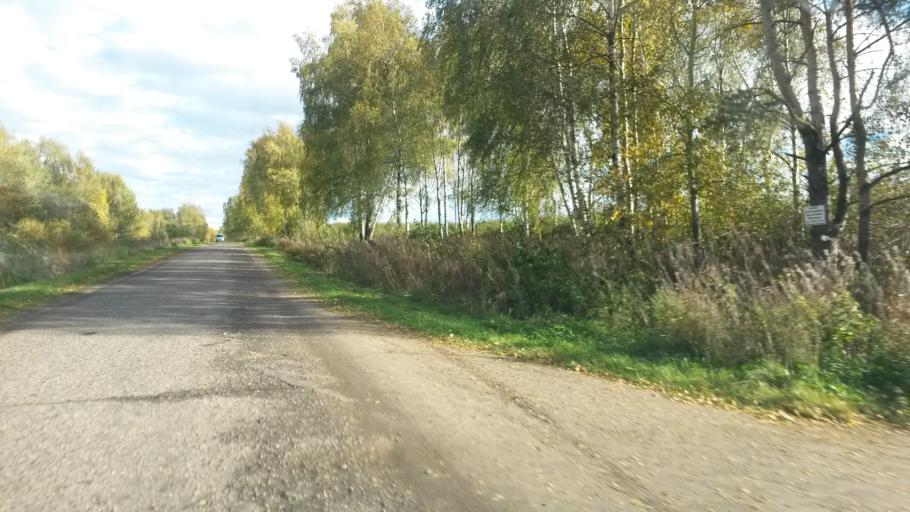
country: RU
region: Jaroslavl
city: Tunoshna
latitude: 57.5258
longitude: 40.0021
